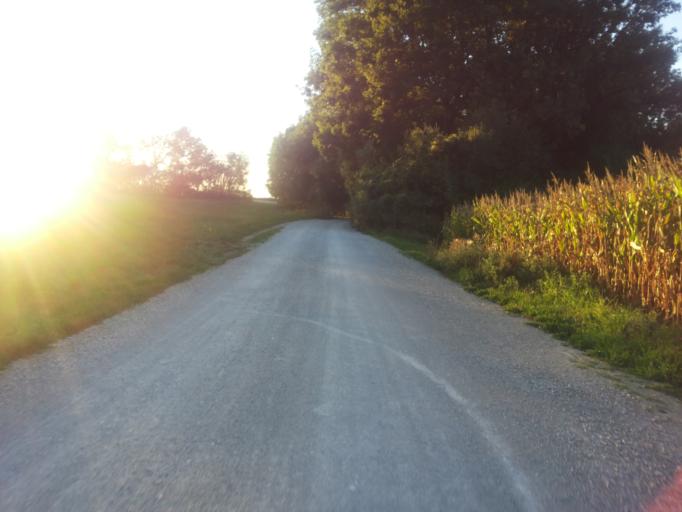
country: DE
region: Bavaria
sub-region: Upper Bavaria
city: Ingolstadt
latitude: 48.7540
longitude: 11.3734
